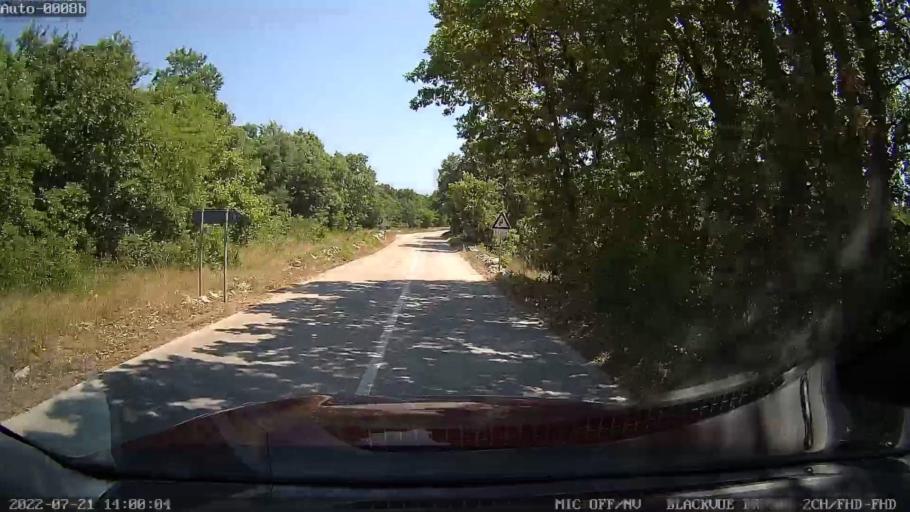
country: HR
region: Istarska
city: Vodnjan
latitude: 45.1007
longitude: 13.8669
